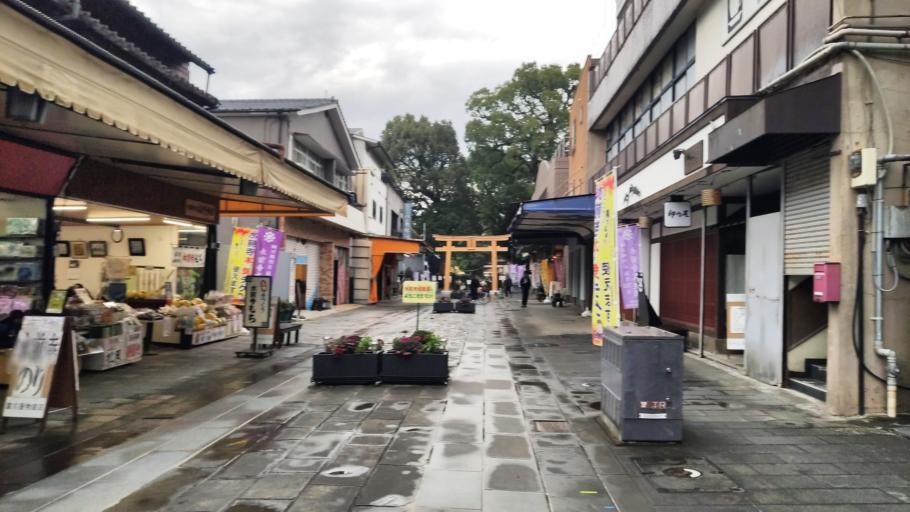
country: JP
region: Kumamoto
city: Kumamoto
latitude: 32.7911
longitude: 130.7325
